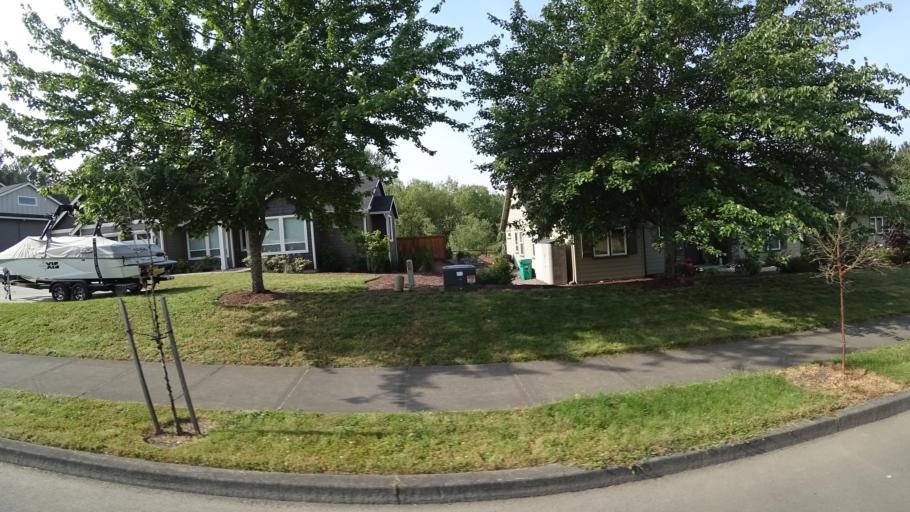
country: US
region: Oregon
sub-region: Clackamas County
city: Happy Valley
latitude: 45.4468
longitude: -122.5187
